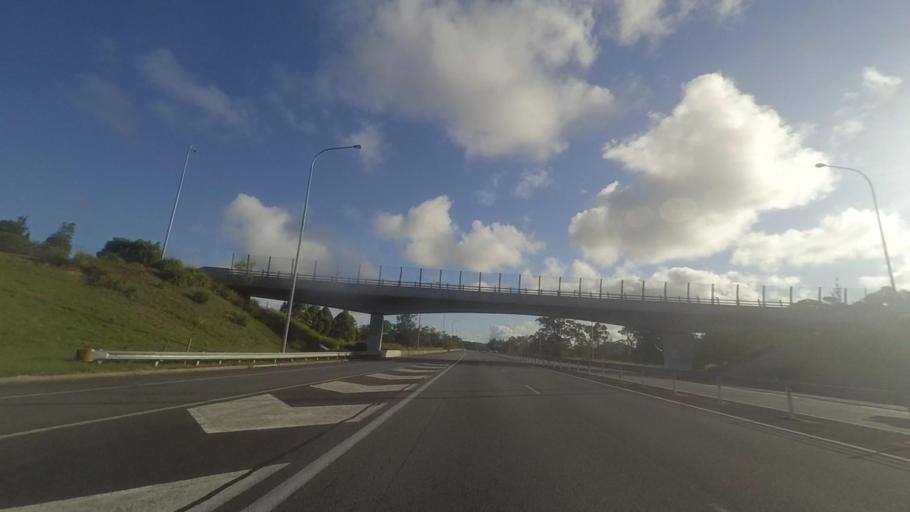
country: AU
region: New South Wales
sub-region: Great Lakes
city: Nabiac
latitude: -32.1010
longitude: 152.3753
